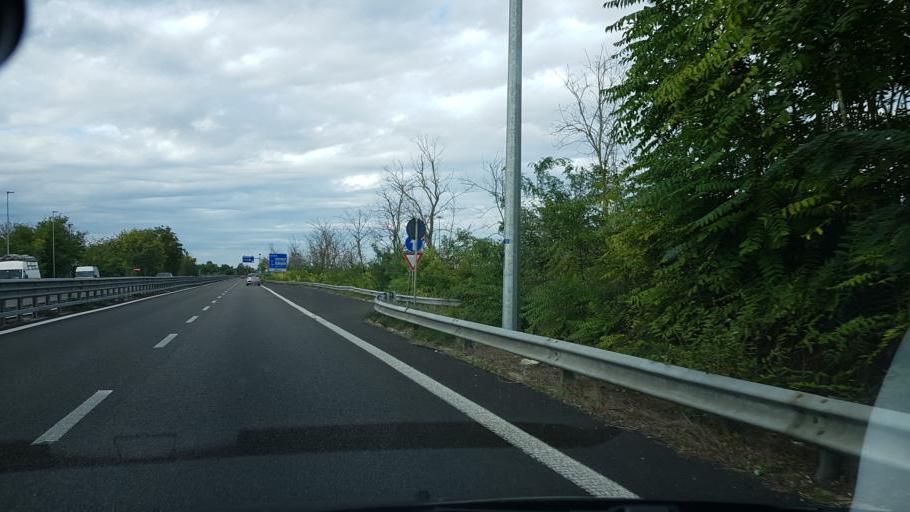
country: IT
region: Apulia
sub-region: Provincia di Lecce
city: Castromediano
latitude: 40.3203
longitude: 18.1872
